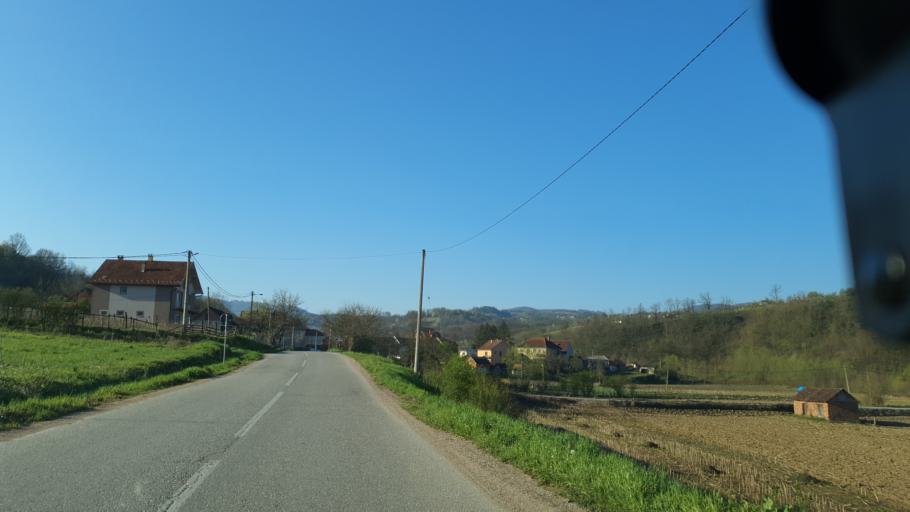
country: RS
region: Central Serbia
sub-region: Kolubarski Okrug
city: Osecina
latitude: 44.3265
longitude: 19.5255
